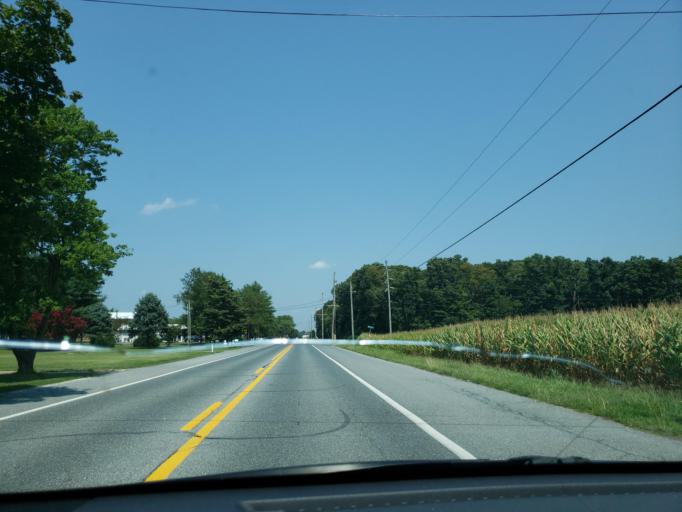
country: US
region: Delaware
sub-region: Sussex County
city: Milton
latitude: 38.7981
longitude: -75.3145
